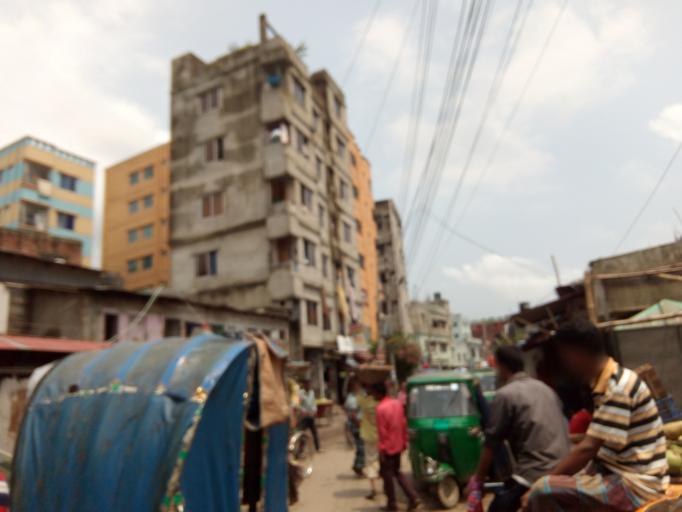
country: BD
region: Dhaka
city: Azimpur
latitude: 23.7456
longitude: 90.3632
